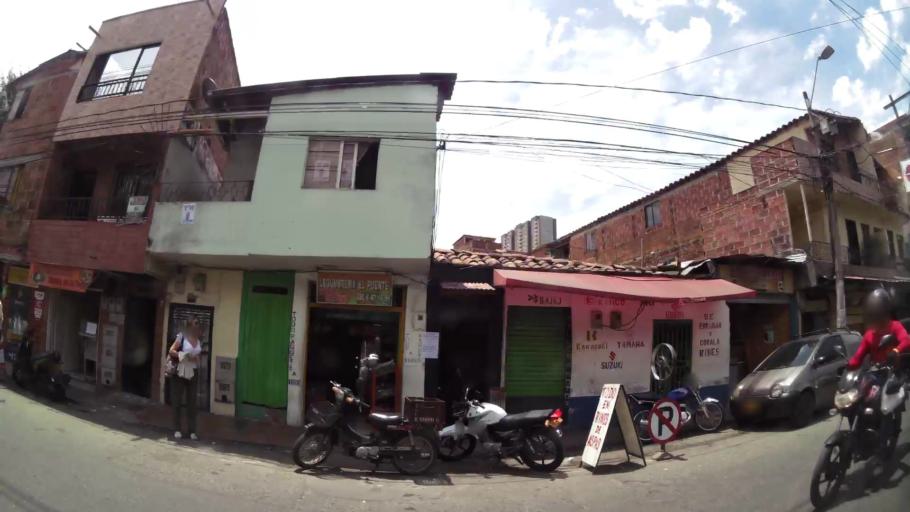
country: CO
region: Antioquia
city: Bello
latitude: 6.3443
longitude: -75.5640
